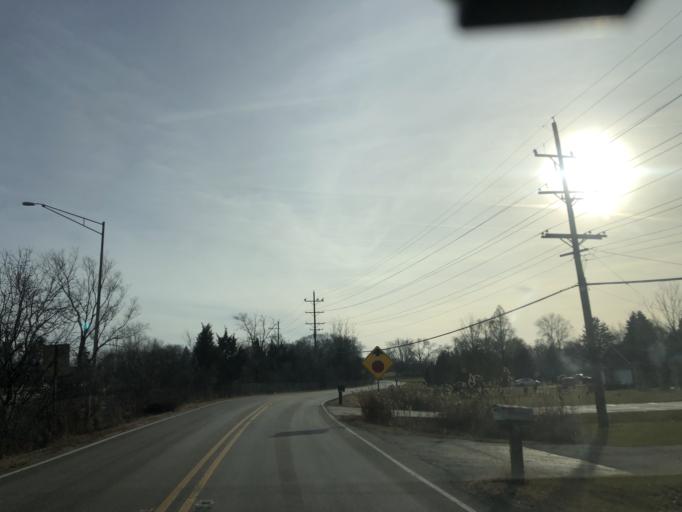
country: US
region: Illinois
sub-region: Cook County
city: Lemont
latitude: 41.7128
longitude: -88.0071
